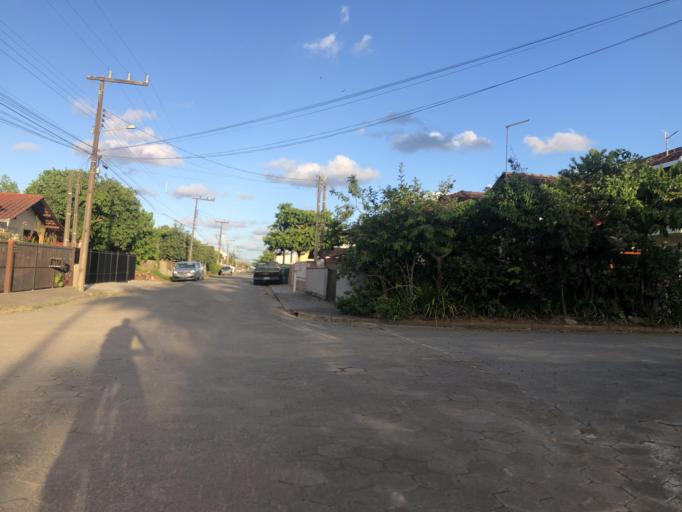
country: BR
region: Santa Catarina
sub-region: Sao Francisco Do Sul
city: Sao Francisco do Sul
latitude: -26.2197
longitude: -48.5309
